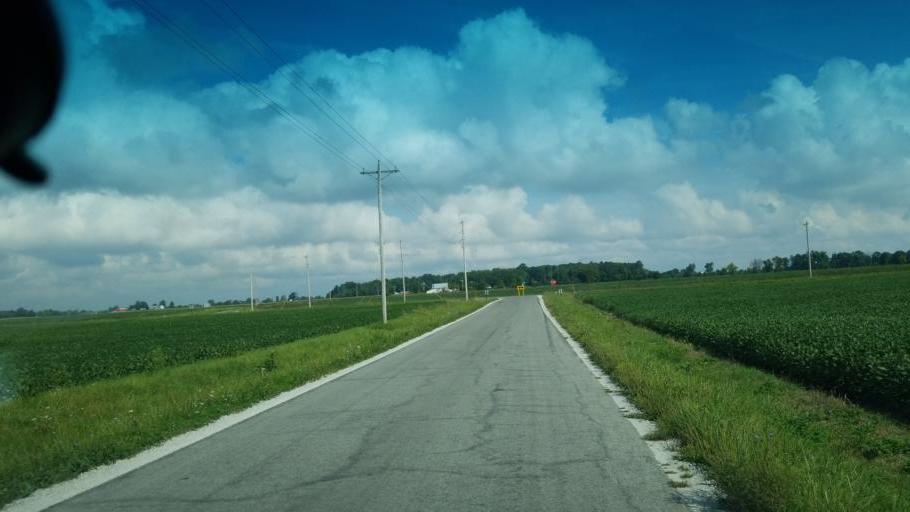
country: US
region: Ohio
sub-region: Wyandot County
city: Carey
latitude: 40.9037
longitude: -83.3992
